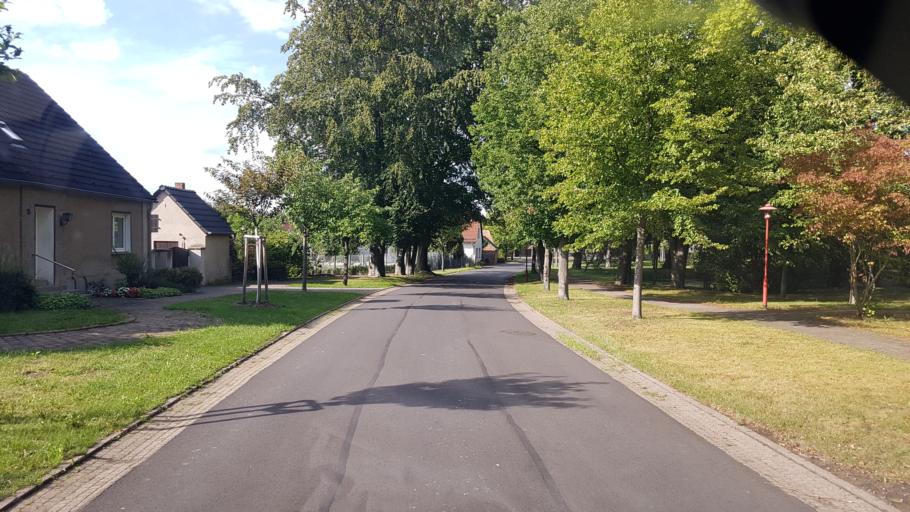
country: DE
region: Saxony
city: Schleife
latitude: 51.5746
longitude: 14.4732
